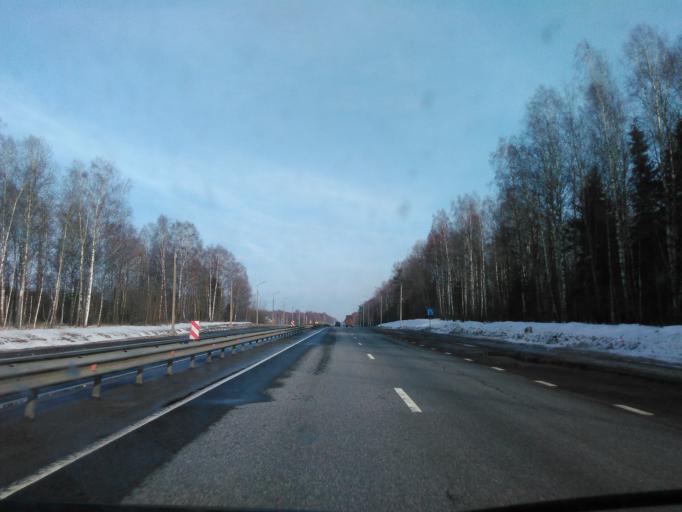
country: RU
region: Smolensk
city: Kholm-Zhirkovskiy
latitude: 55.1897
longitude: 33.7639
